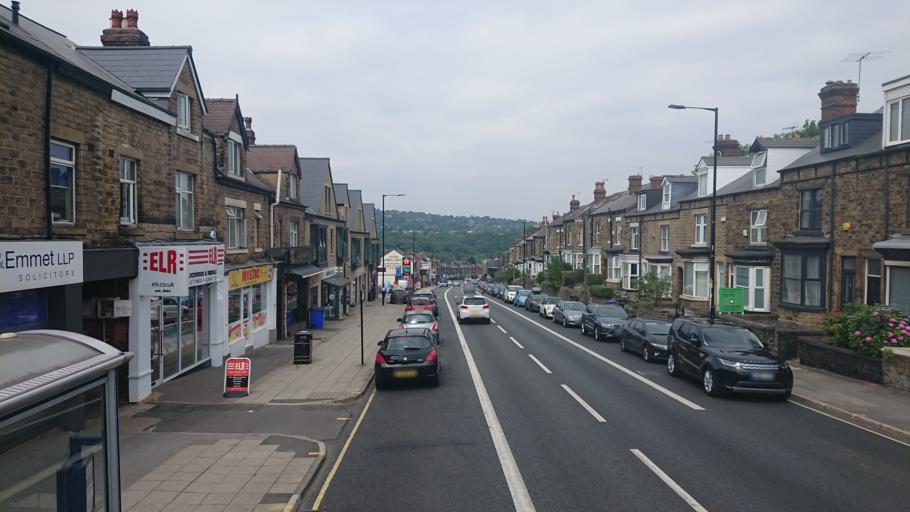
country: GB
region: England
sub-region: Sheffield
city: Sheffield
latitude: 53.3622
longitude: -1.5083
